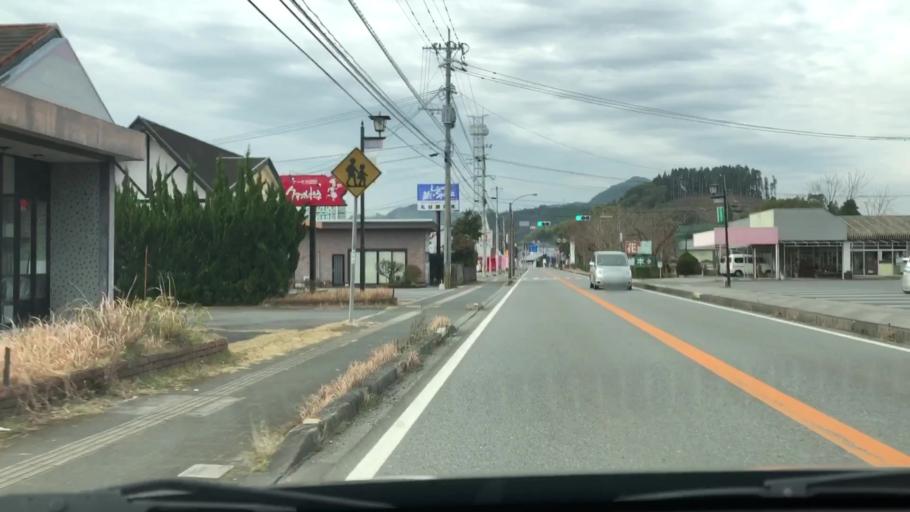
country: JP
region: Oita
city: Saiki
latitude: 32.9713
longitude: 131.8404
